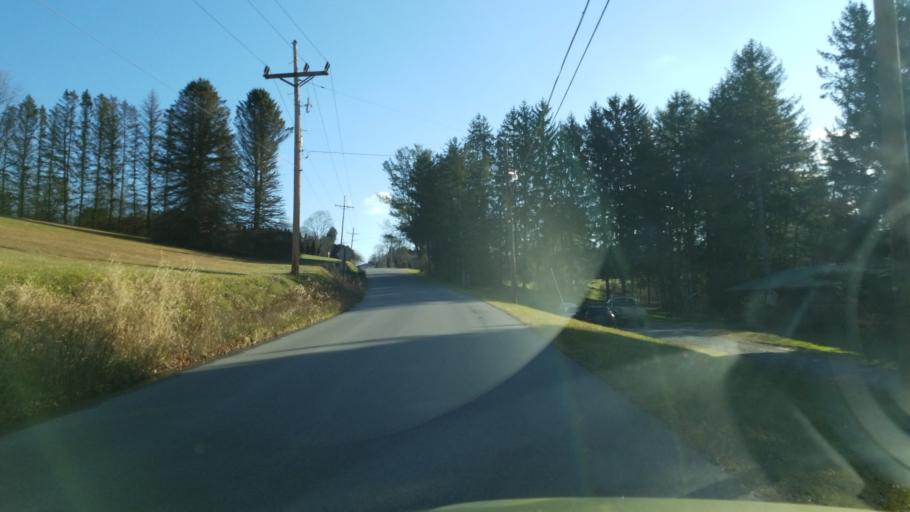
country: US
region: Pennsylvania
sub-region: Clearfield County
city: Clearfield
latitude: 41.0162
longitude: -78.4258
